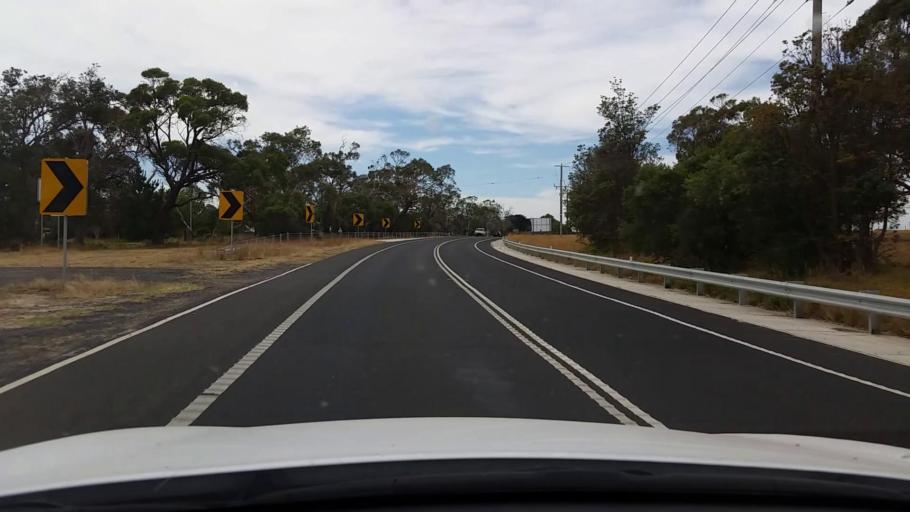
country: AU
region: Victoria
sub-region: Mornington Peninsula
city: Safety Beach
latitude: -38.3157
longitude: 145.0188
